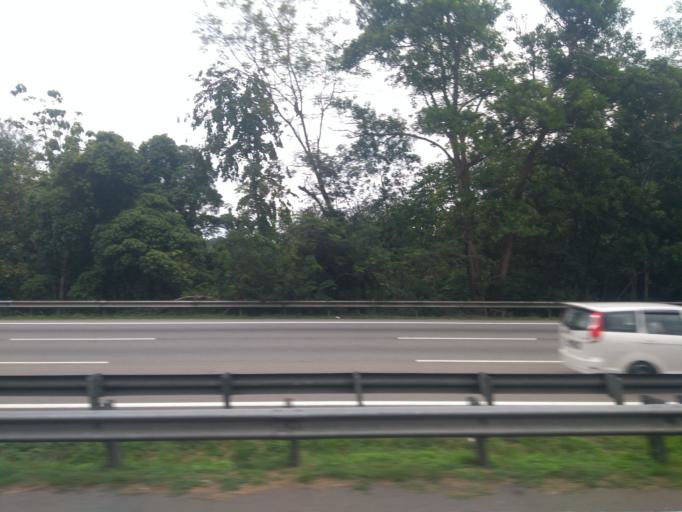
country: MY
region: Melaka
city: Pulau Sebang
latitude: 2.4477
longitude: 102.1732
